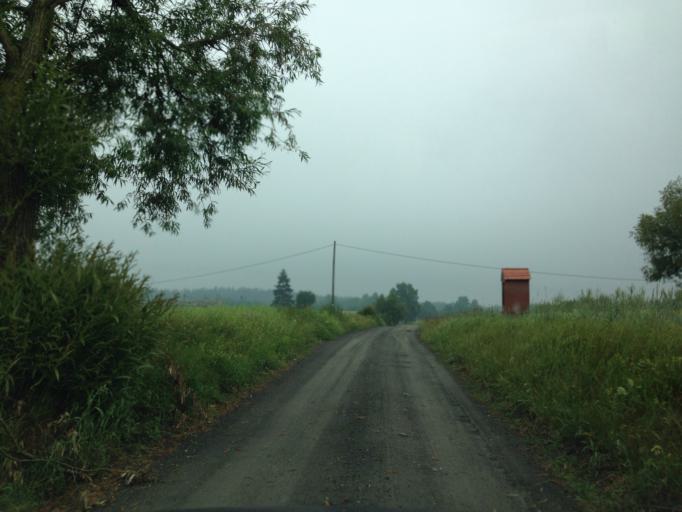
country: PL
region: Kujawsko-Pomorskie
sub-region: Powiat brodnicki
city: Brodnica
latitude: 53.3114
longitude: 19.3608
